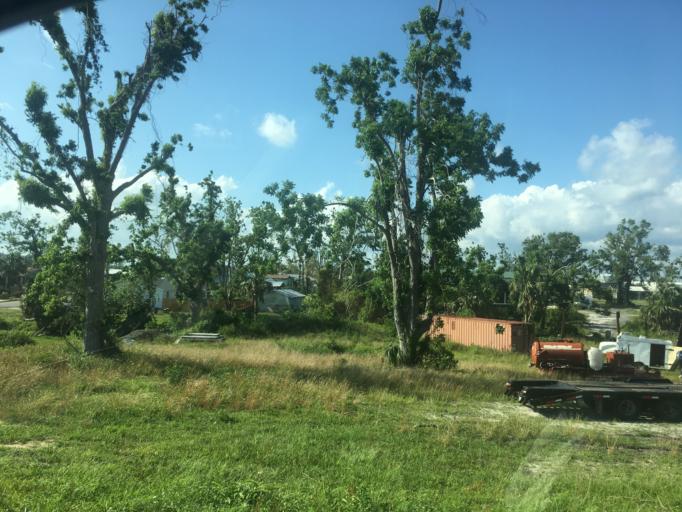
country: US
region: Florida
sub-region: Bay County
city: Cedar Grove
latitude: 30.1532
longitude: -85.6348
